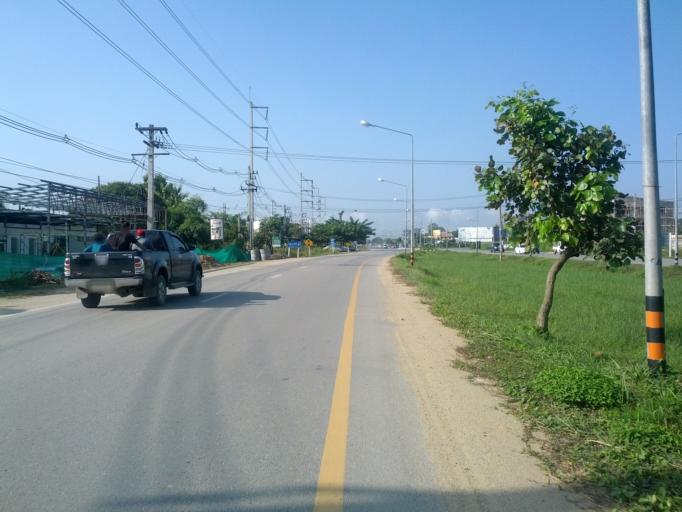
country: TH
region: Chiang Mai
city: Saraphi
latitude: 18.7553
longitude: 99.0602
